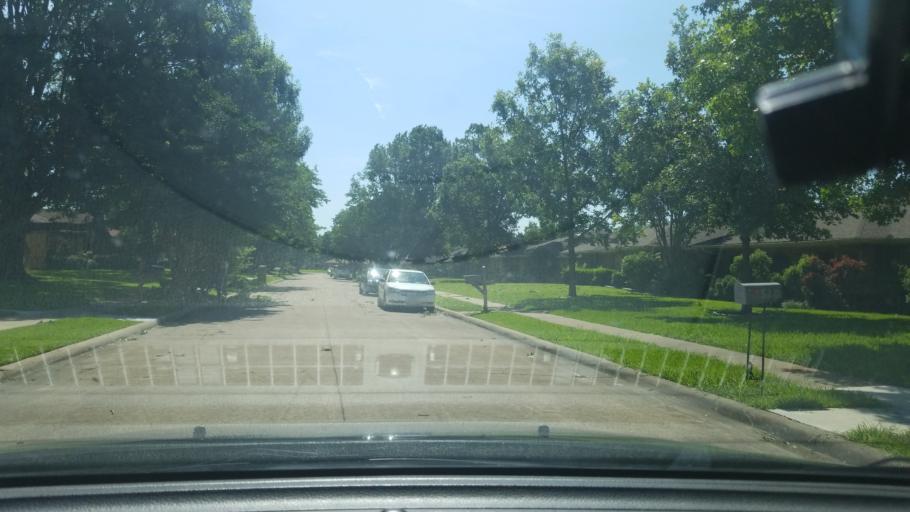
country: US
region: Texas
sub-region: Dallas County
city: Mesquite
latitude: 32.7726
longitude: -96.5939
